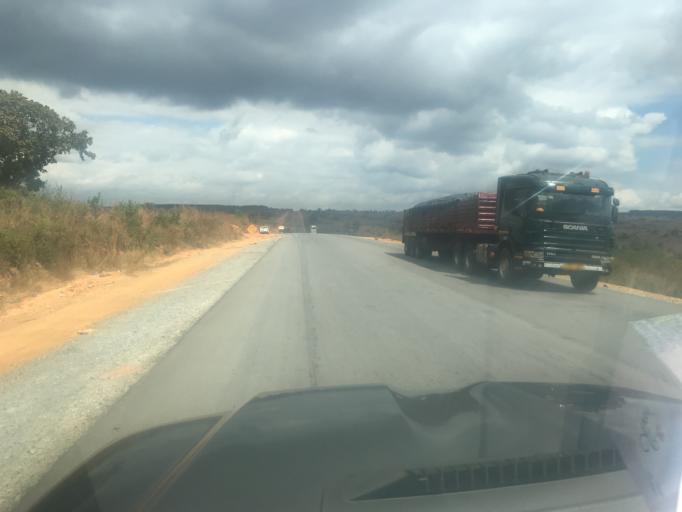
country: TZ
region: Iringa
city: Makungu
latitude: -8.3483
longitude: 35.2441
